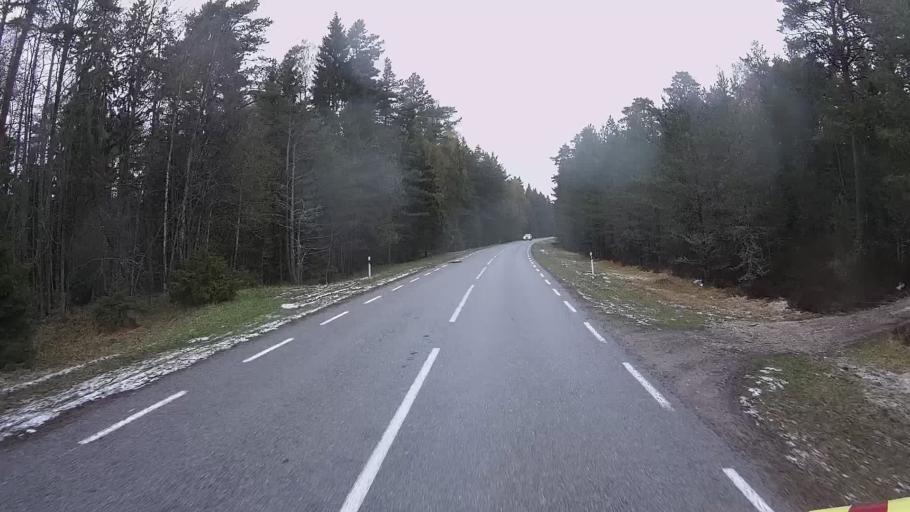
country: EE
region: Hiiumaa
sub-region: Kaerdla linn
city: Kardla
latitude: 59.0528
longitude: 22.6817
